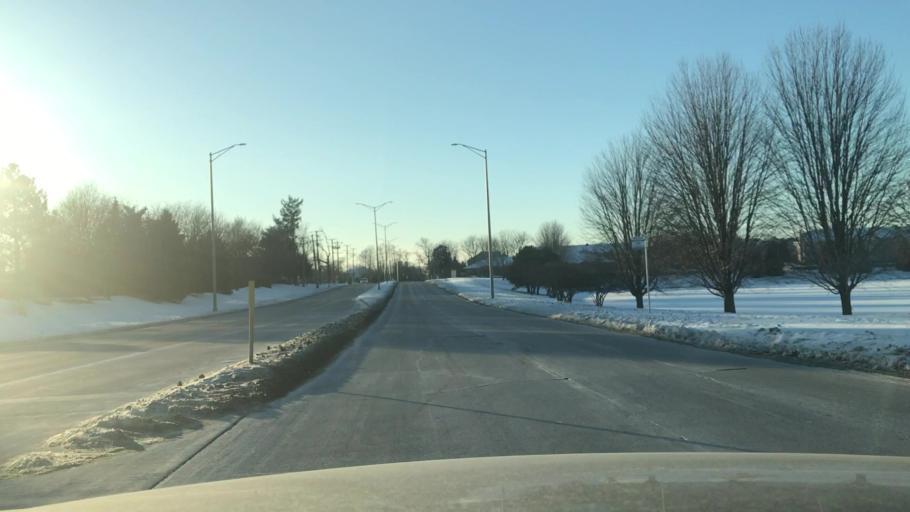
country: US
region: Illinois
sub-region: Kane County
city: Aurora
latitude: 41.7591
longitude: -88.2459
